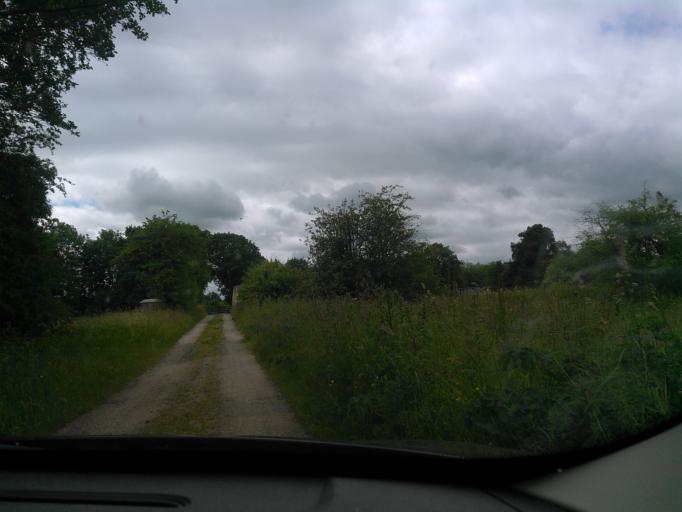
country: GB
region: England
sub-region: Shropshire
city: Whitchurch
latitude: 52.9258
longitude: -2.7391
